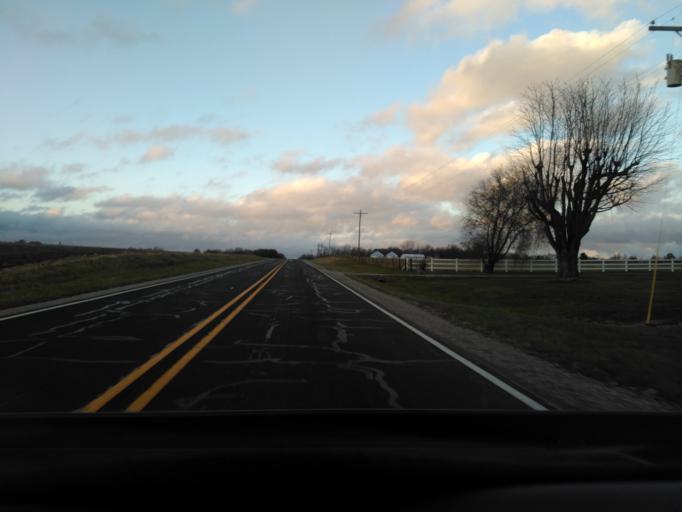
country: US
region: Illinois
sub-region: Effingham County
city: Altamont
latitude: 38.9721
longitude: -88.7489
